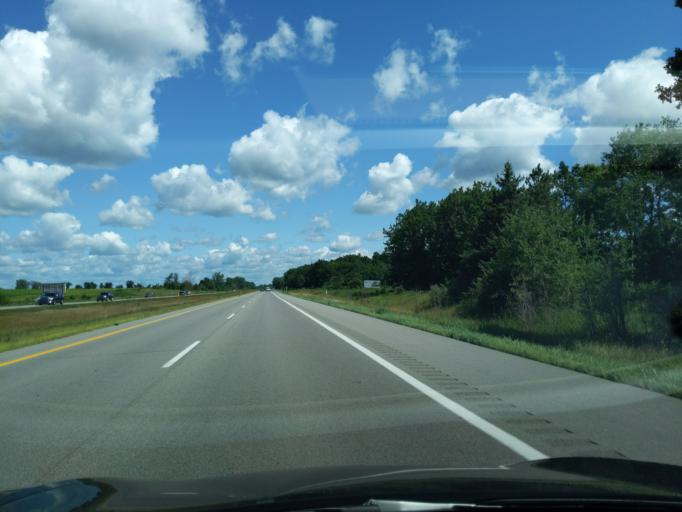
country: US
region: Michigan
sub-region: Isabella County
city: Shepherd
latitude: 43.4826
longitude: -84.6778
